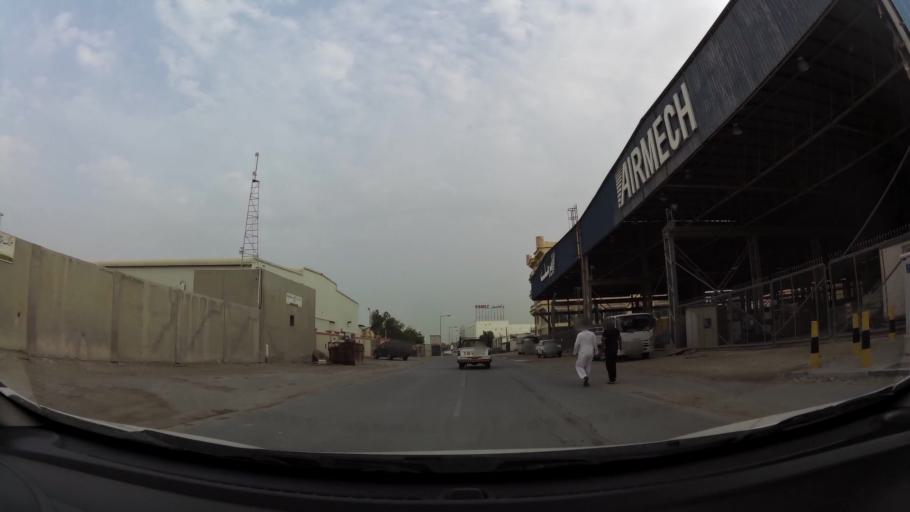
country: BH
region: Northern
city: Ar Rifa'
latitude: 26.1261
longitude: 50.5872
